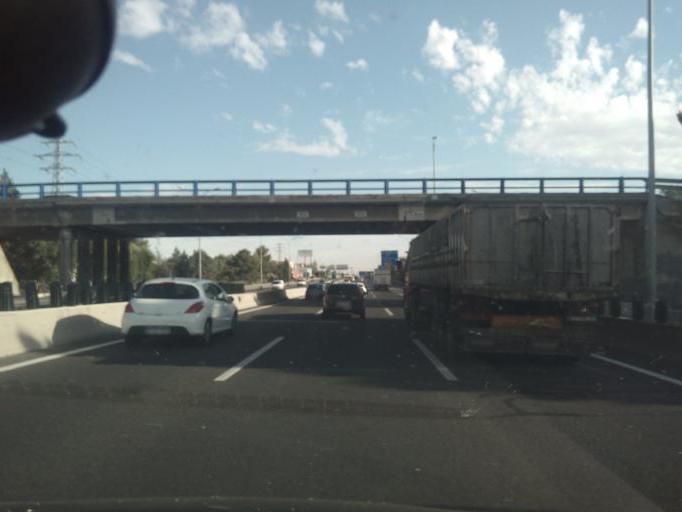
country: ES
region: Madrid
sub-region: Provincia de Madrid
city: Pinto
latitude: 40.2456
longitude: -3.6899
